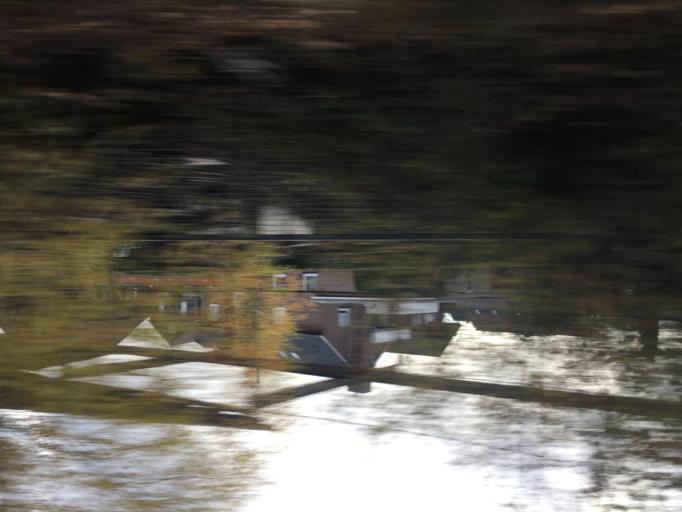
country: DE
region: North Rhine-Westphalia
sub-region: Regierungsbezirk Munster
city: Steinfurt
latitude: 52.1174
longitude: 7.4044
